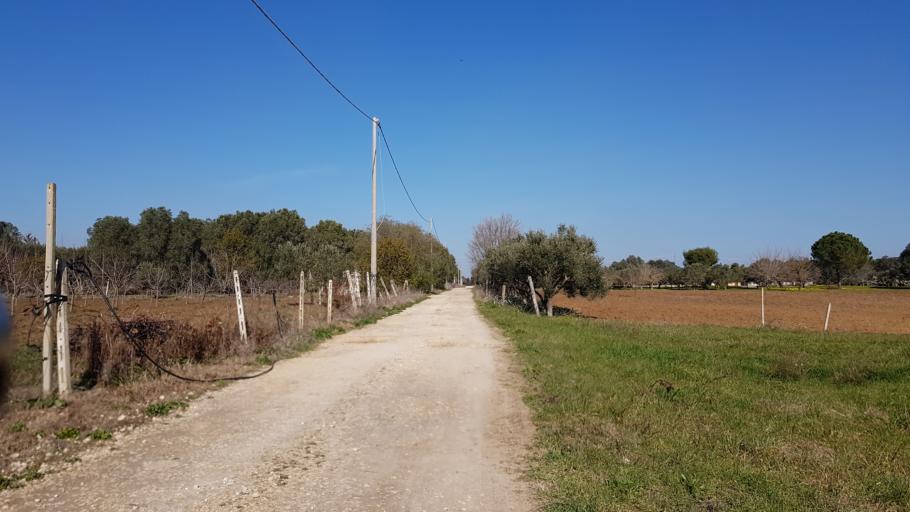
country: IT
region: Apulia
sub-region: Provincia di Brindisi
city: Mesagne
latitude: 40.6139
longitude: 17.8046
